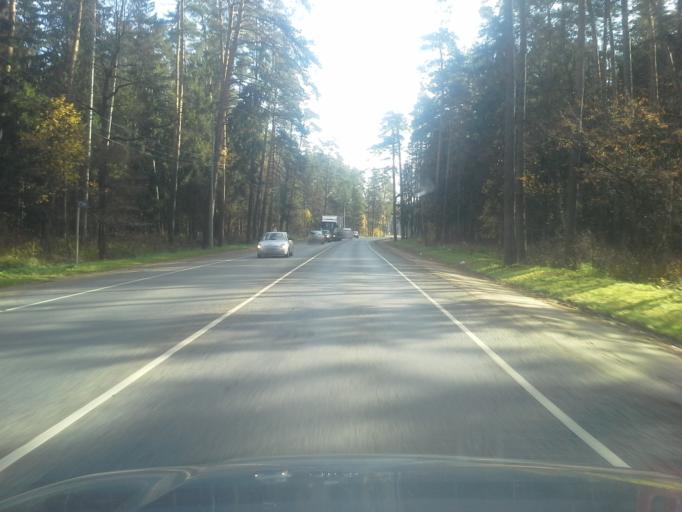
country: RU
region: Moskovskaya
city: Bol'shiye Vyazemy
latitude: 55.6770
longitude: 36.9268
